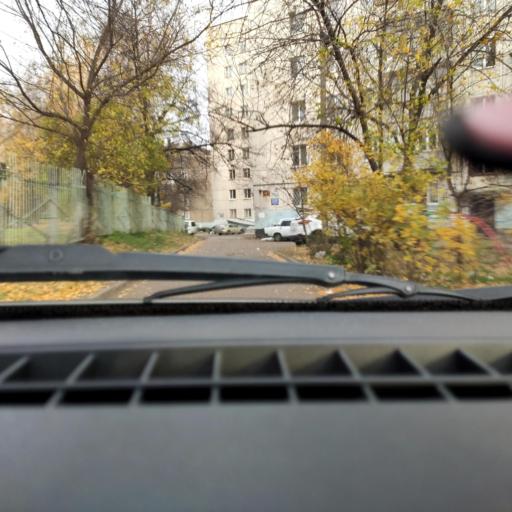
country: RU
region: Bashkortostan
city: Ufa
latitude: 54.8012
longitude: 56.1289
